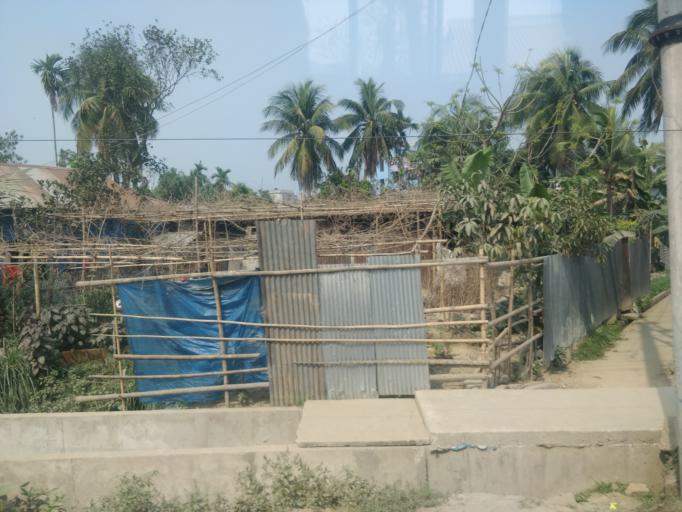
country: BD
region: Sylhet
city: Habiganj
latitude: 24.3656
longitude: 91.4162
